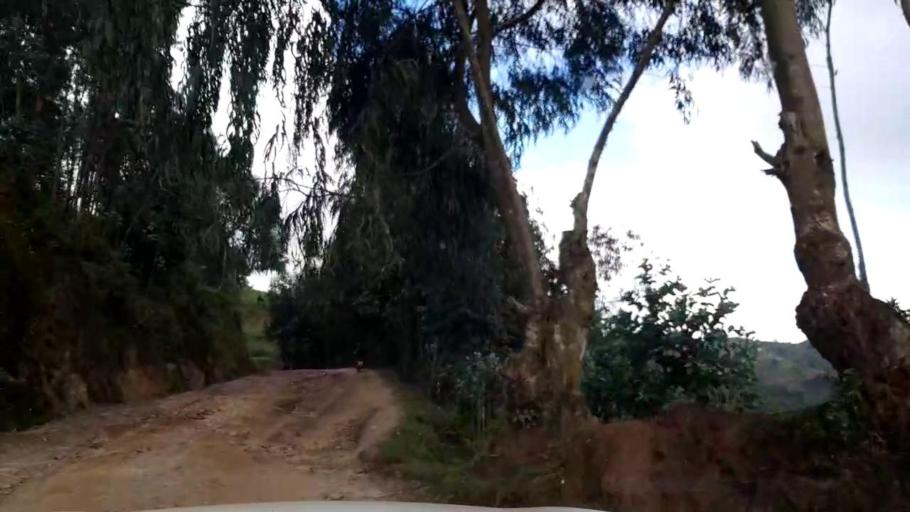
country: RW
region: Western Province
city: Kibuye
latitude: -1.8925
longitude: 29.4633
